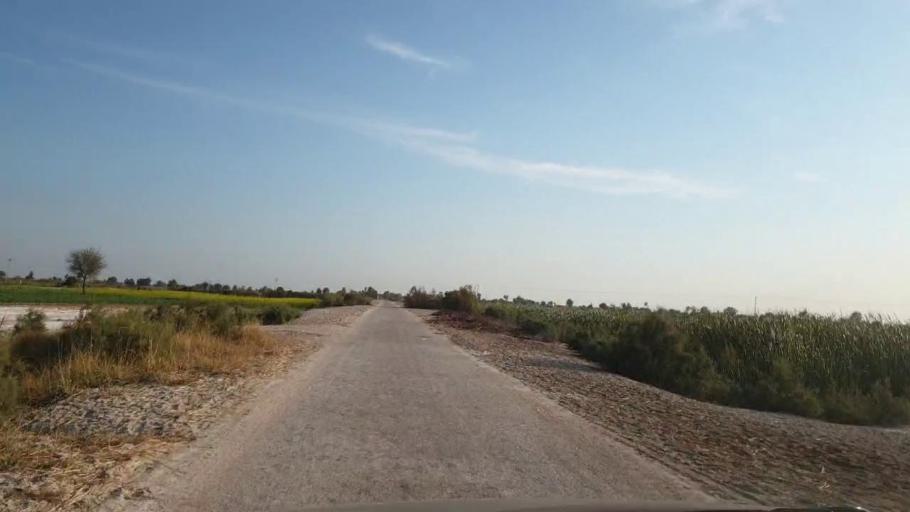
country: PK
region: Sindh
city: Khadro
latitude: 26.2075
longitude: 68.7461
